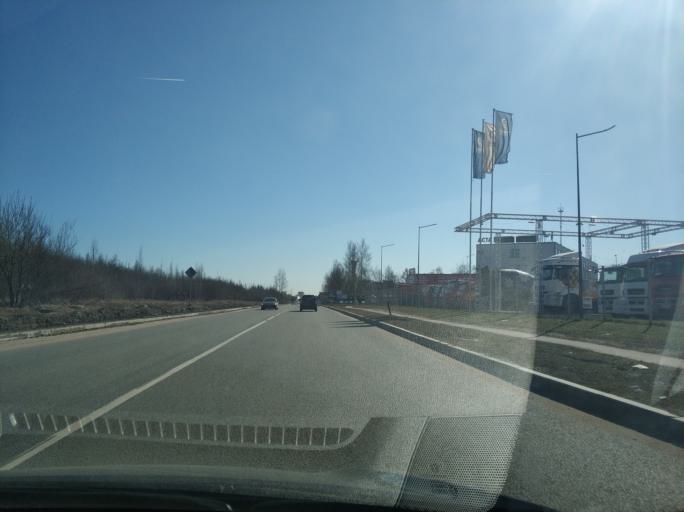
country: RU
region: Leningrad
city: Bugry
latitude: 60.0739
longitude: 30.3787
